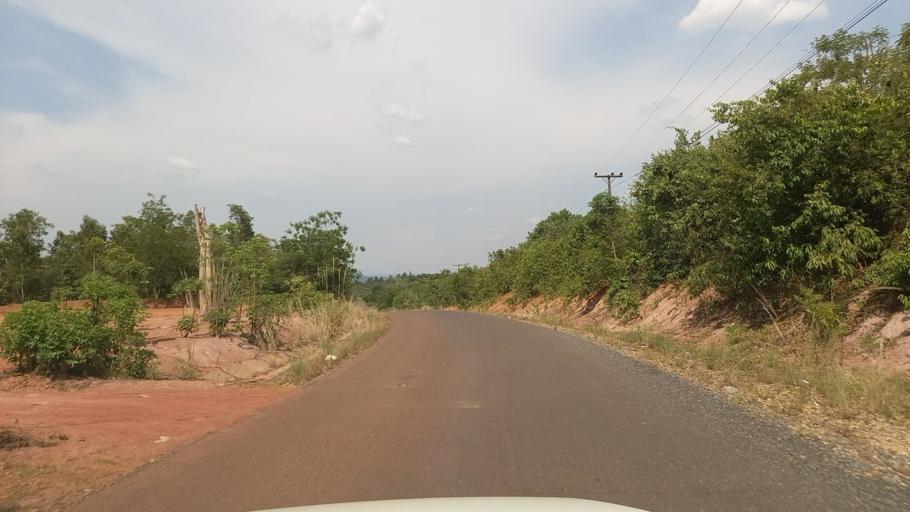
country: LA
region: Bolikhamxai
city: Muang Pakxan
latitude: 18.4287
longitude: 103.7320
